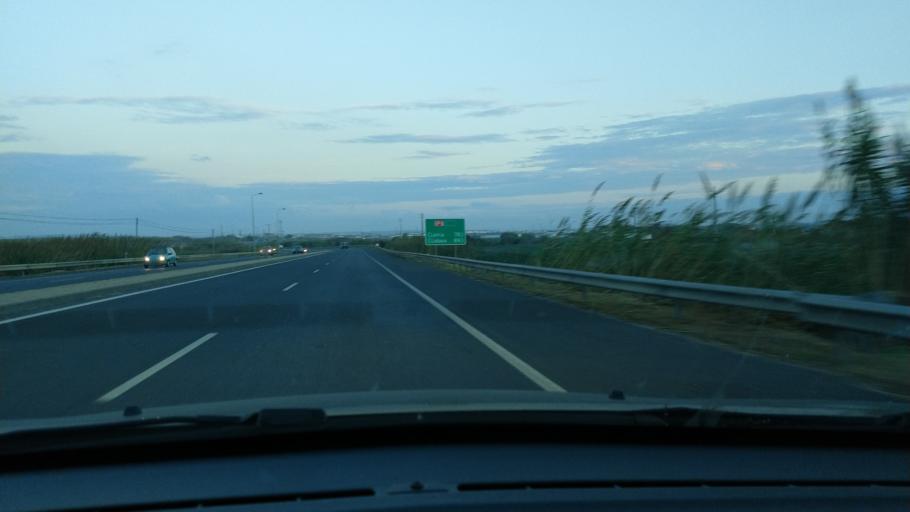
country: PT
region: Leiria
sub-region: Peniche
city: Atouguia da Baleia
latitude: 39.3485
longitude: -9.3508
